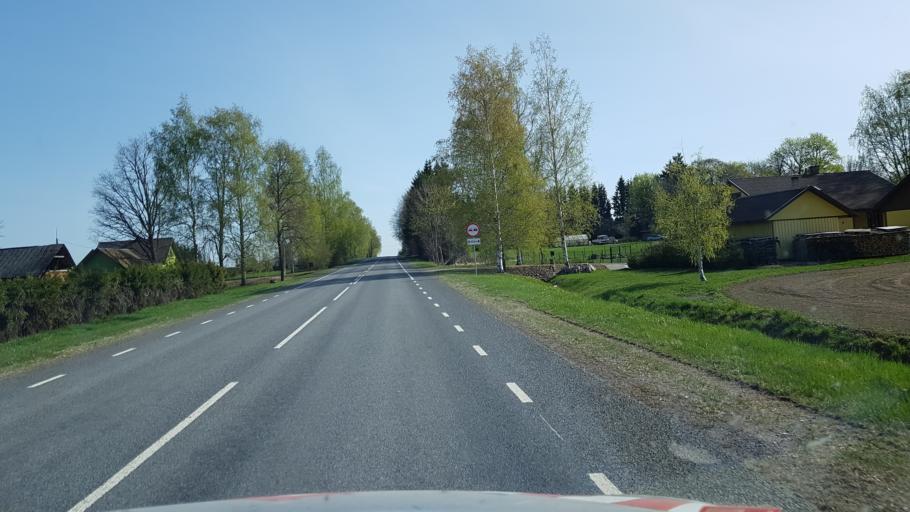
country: EE
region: Viljandimaa
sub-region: Karksi vald
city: Karksi-Nuia
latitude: 58.1825
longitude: 25.5041
